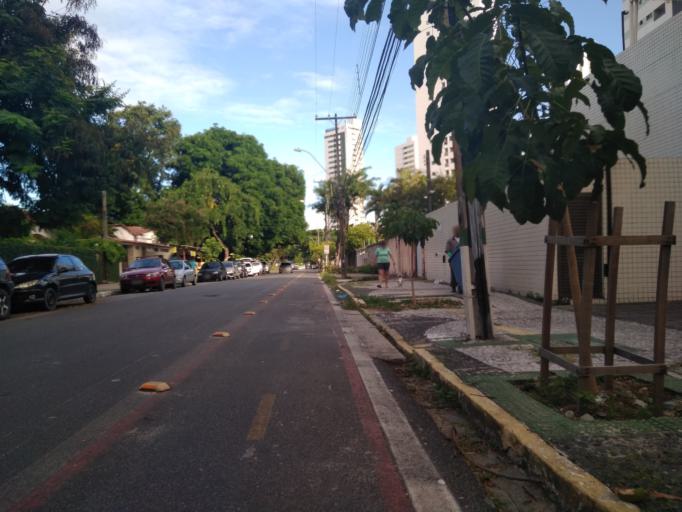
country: BR
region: Pernambuco
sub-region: Recife
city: Recife
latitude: -8.0337
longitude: -34.8948
